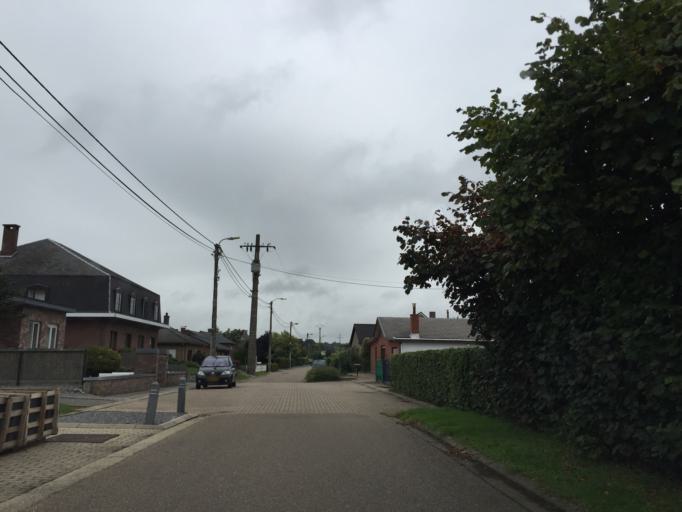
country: NL
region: Limburg
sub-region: Eijsden-Margraten
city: Eijsden
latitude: 50.7594
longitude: 5.7186
